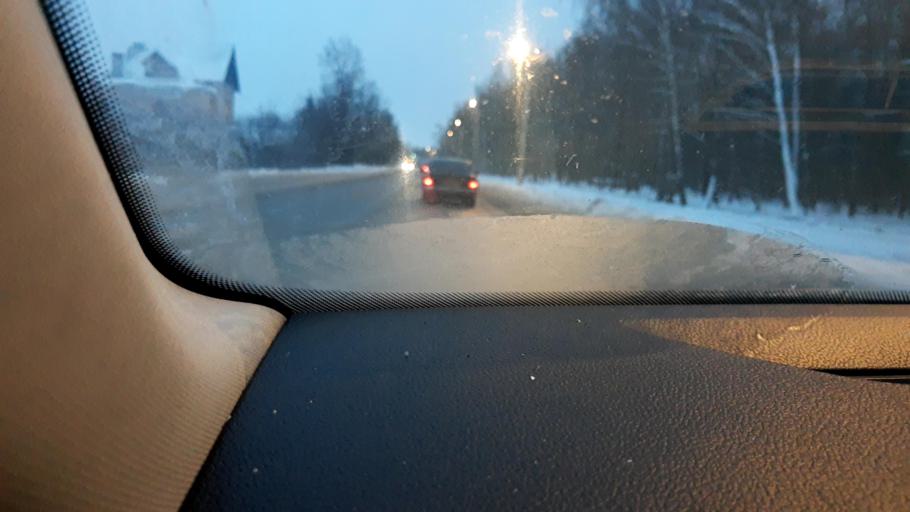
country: RU
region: Moskovskaya
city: Troitsk
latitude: 55.3097
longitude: 37.1780
